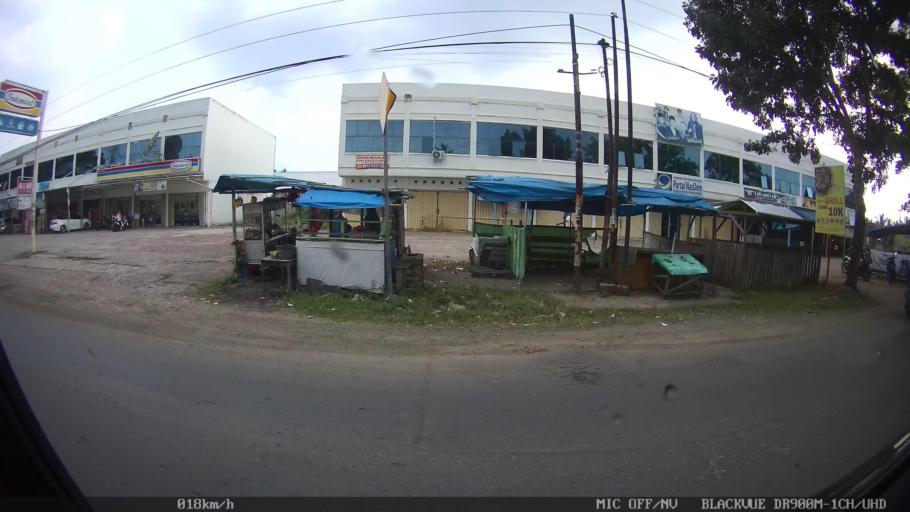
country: ID
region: Lampung
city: Gadingrejo
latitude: -5.3723
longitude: 105.0775
